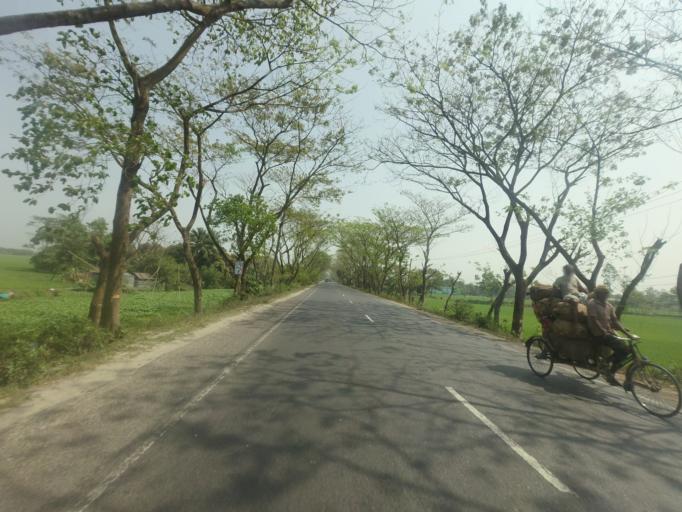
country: BD
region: Dhaka
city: Bhairab Bazar
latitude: 24.0465
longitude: 91.0815
